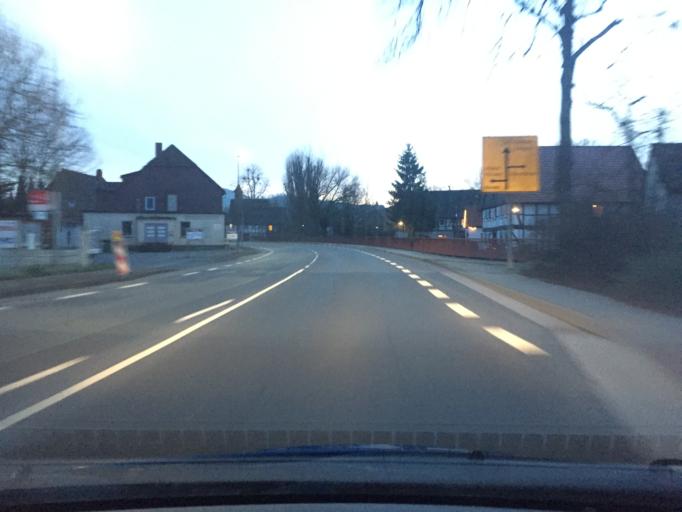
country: DE
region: Lower Saxony
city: Luerdissen
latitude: 51.9397
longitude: 9.6327
